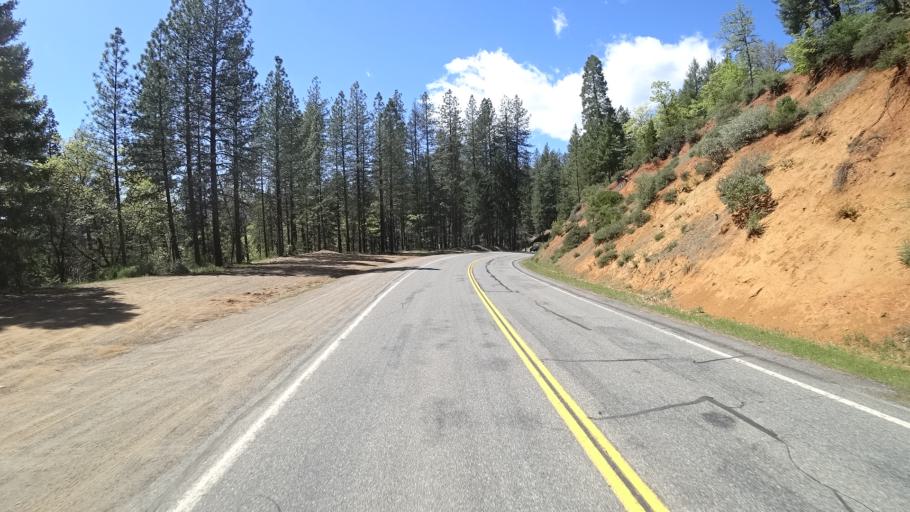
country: US
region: California
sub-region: Trinity County
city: Weaverville
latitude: 40.7560
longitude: -122.9093
